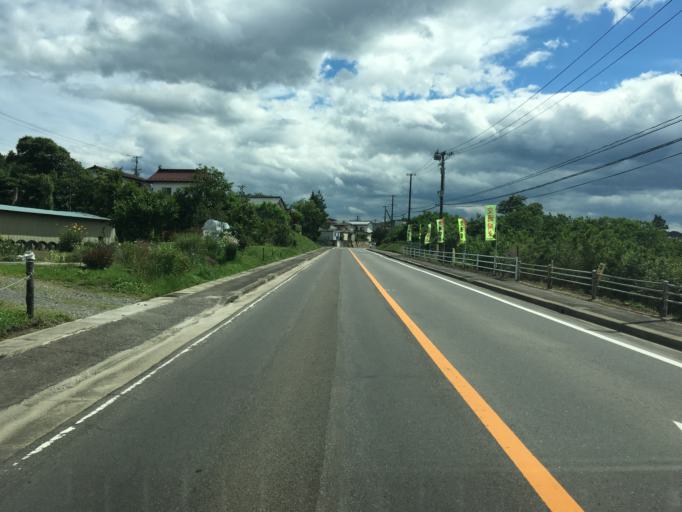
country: JP
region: Fukushima
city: Fukushima-shi
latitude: 37.6609
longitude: 140.5448
